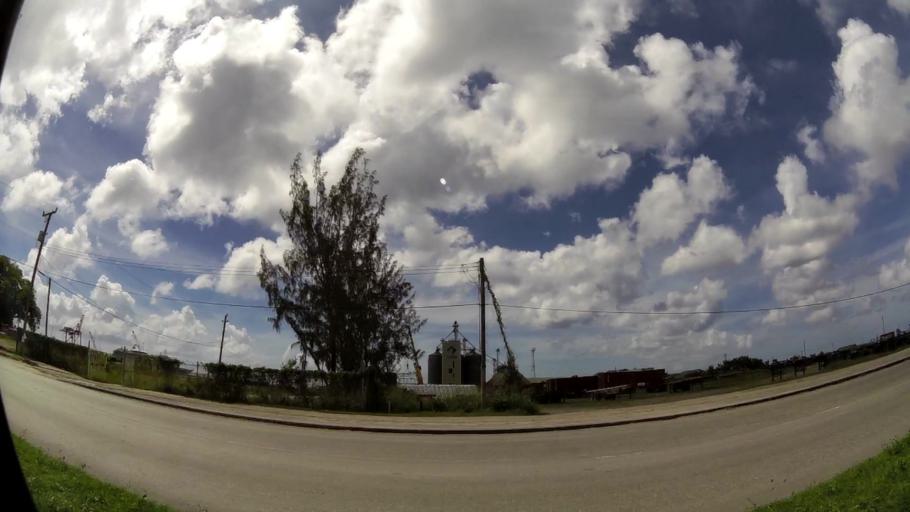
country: BB
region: Saint Michael
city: Bridgetown
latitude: 13.1112
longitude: -59.6269
